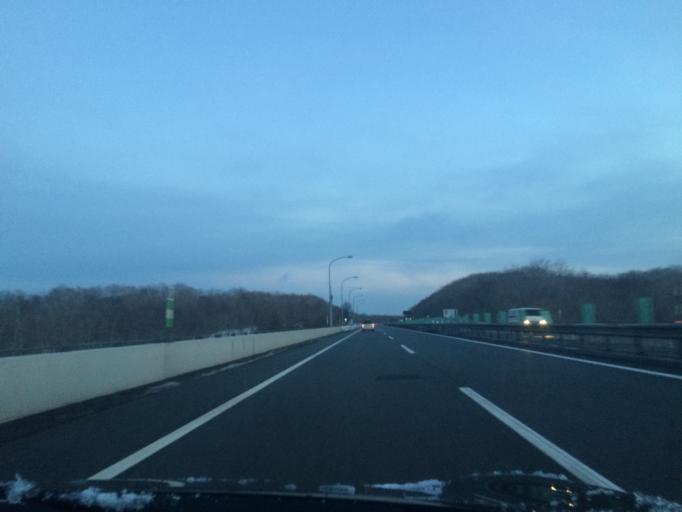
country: JP
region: Hokkaido
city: Chitose
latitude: 42.8061
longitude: 141.6235
